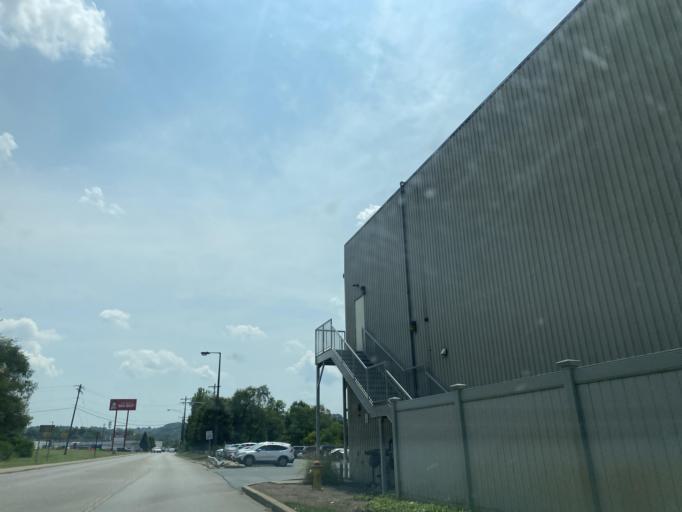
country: US
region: Kentucky
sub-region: Campbell County
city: Bellevue
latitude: 39.1006
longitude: -84.4875
